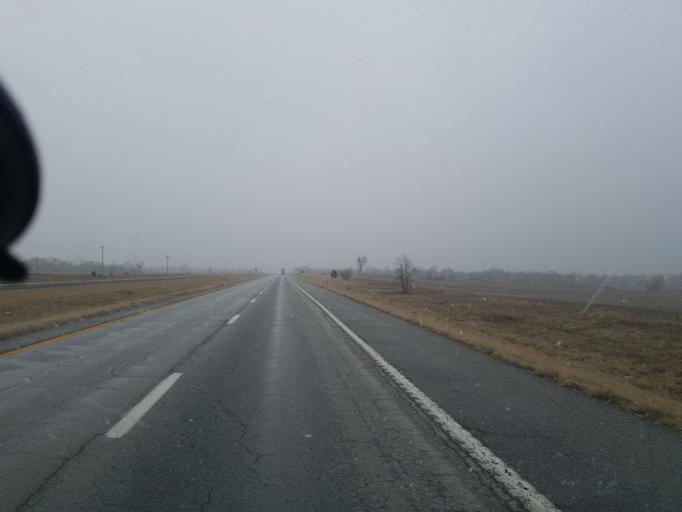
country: US
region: Missouri
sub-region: Macon County
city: La Plata
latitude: 39.9359
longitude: -92.4769
